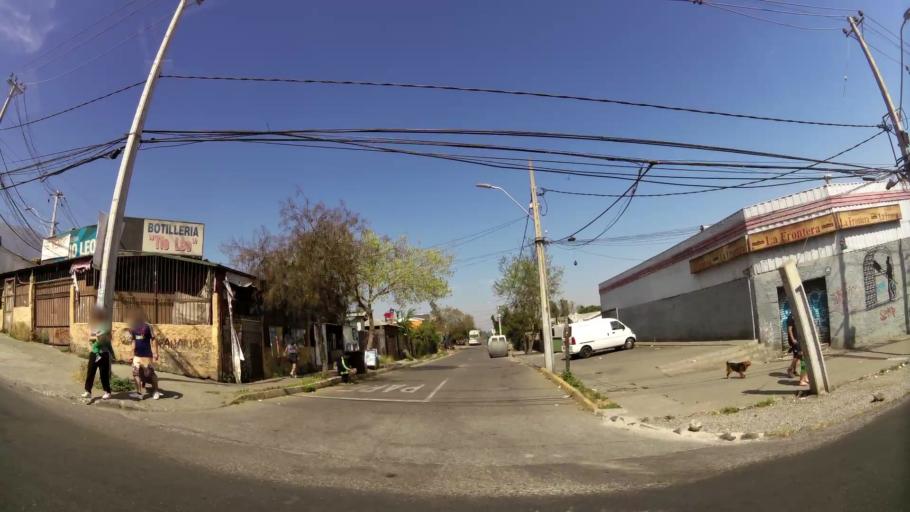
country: CL
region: Santiago Metropolitan
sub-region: Provincia de Santiago
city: Villa Presidente Frei, Nunoa, Santiago, Chile
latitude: -33.4746
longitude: -70.5271
